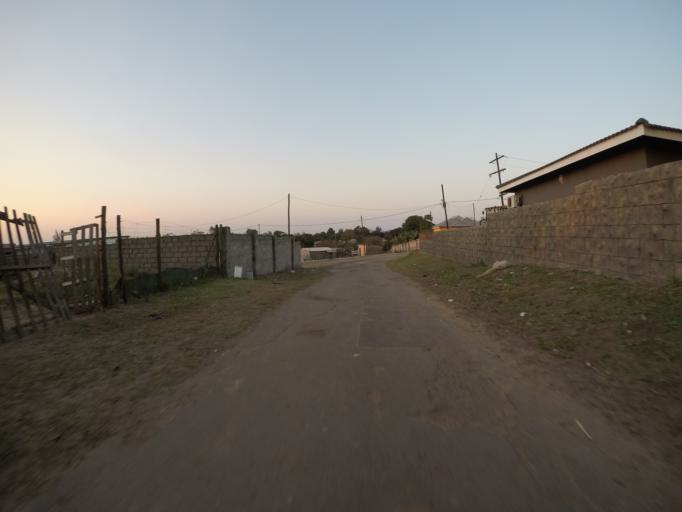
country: ZA
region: KwaZulu-Natal
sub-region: uThungulu District Municipality
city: Richards Bay
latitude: -28.7593
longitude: 32.1268
